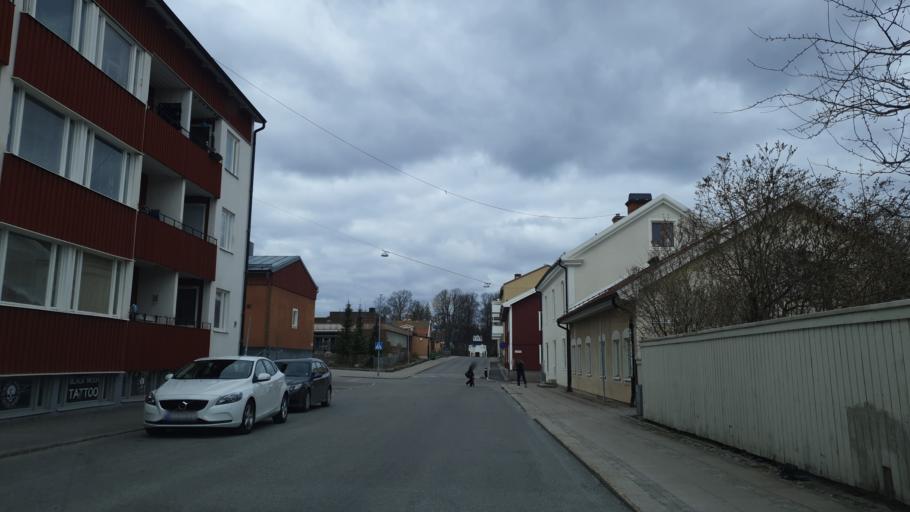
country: SE
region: OErebro
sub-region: Nora Kommun
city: Nora
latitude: 59.5204
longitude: 15.0384
